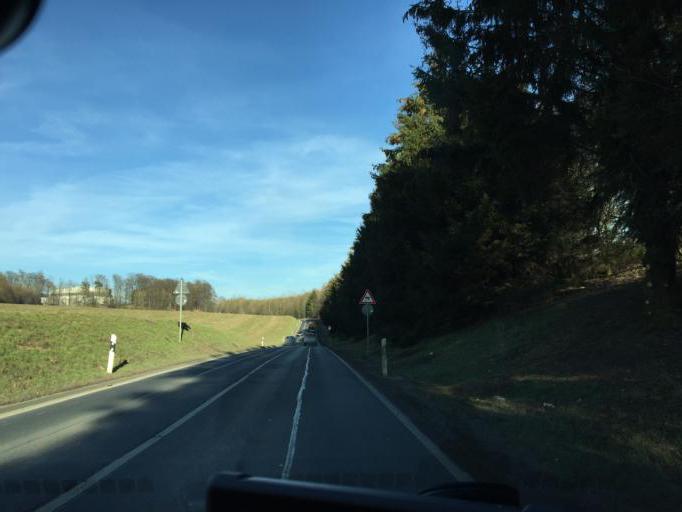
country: DE
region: Rheinland-Pfalz
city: Ruppach-Goldhausen
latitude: 50.4771
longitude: 7.8715
